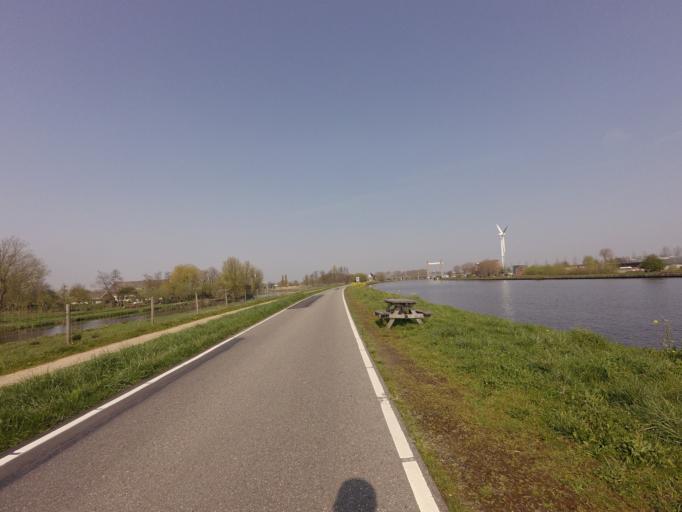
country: NL
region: South Holland
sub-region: Gemeente Gouda
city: Bloemendaal
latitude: 52.0110
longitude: 4.6860
